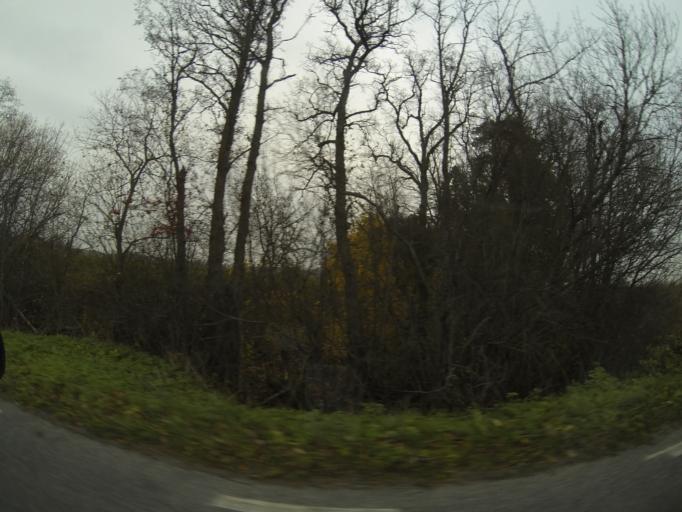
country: SE
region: Vaestmanland
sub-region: Vasteras
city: Skultuna
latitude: 59.6852
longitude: 16.4329
